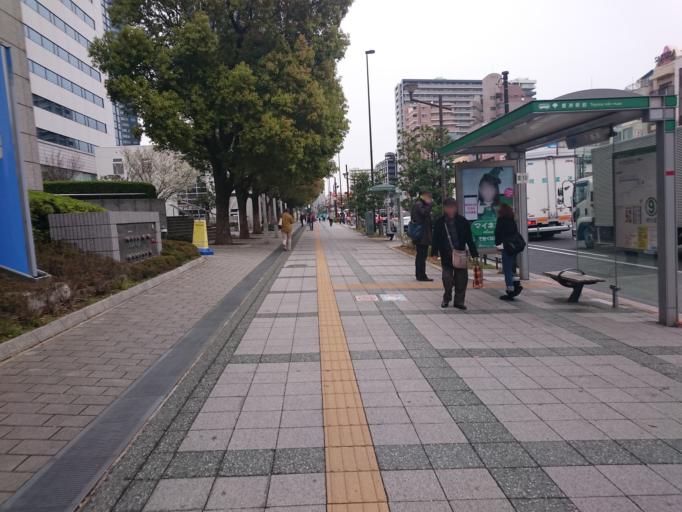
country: JP
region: Tokyo
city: Urayasu
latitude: 35.6552
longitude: 139.7970
